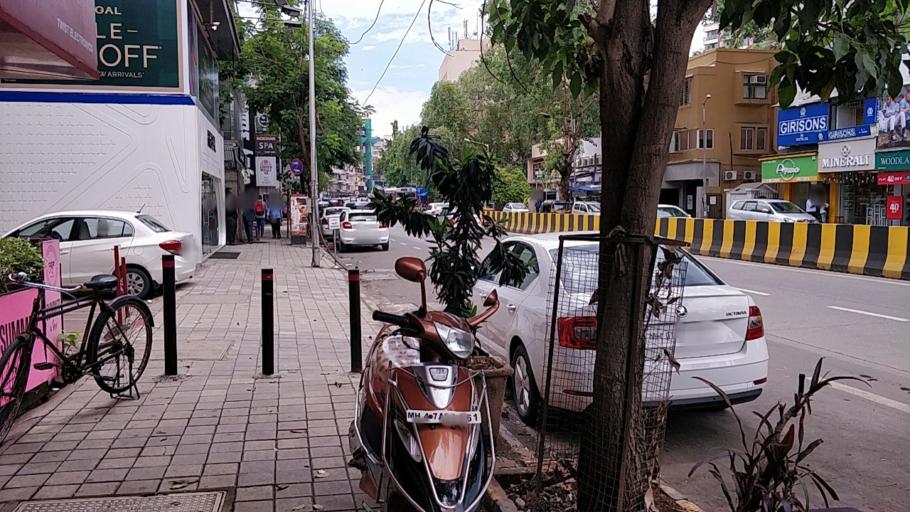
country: IN
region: Maharashtra
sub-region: Mumbai Suburban
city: Mumbai
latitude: 19.0660
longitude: 72.8341
